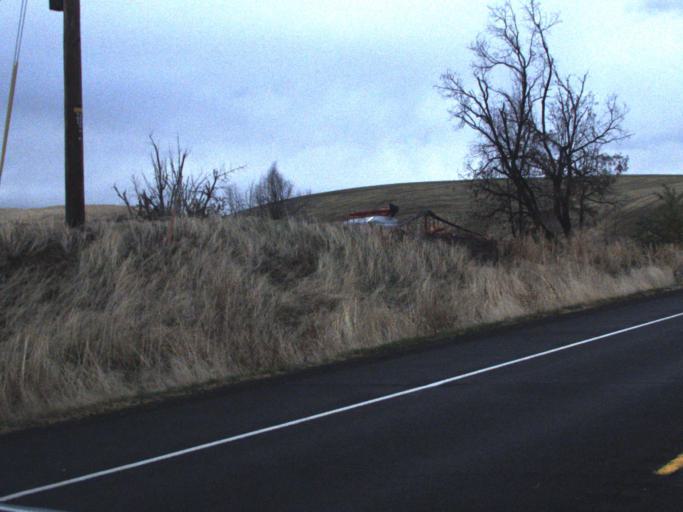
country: US
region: Washington
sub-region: Walla Walla County
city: Walla Walla East
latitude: 46.1274
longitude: -118.1939
